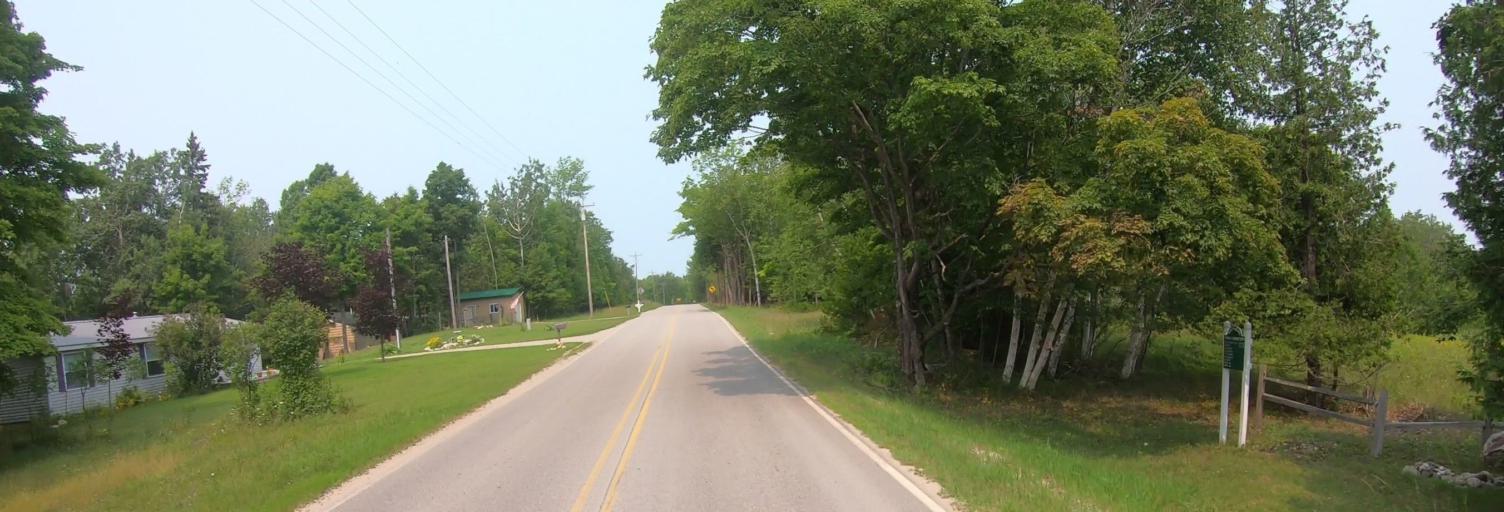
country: CA
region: Ontario
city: Thessalon
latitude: 46.0177
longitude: -83.7182
